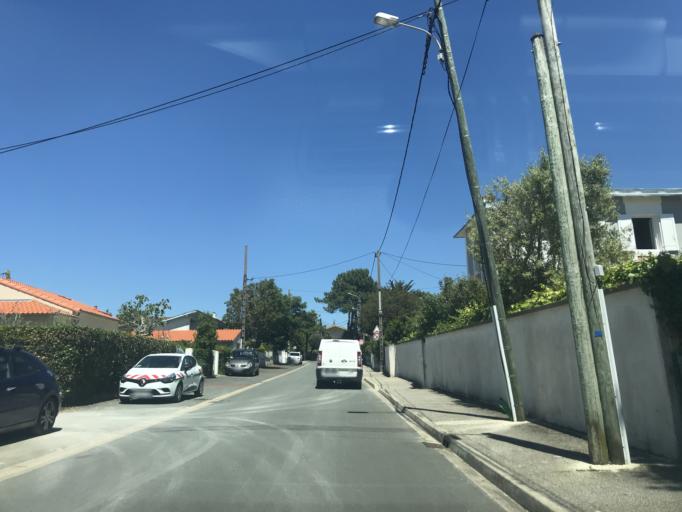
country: FR
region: Poitou-Charentes
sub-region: Departement de la Charente-Maritime
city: Saint-Palais-sur-Mer
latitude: 45.6482
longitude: -1.1096
